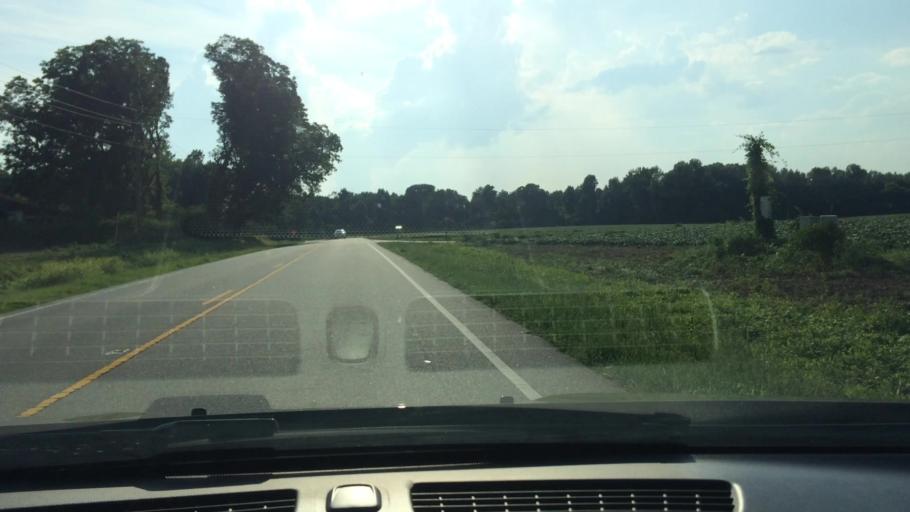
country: US
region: North Carolina
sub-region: Pitt County
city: Ayden
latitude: 35.4718
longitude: -77.3935
